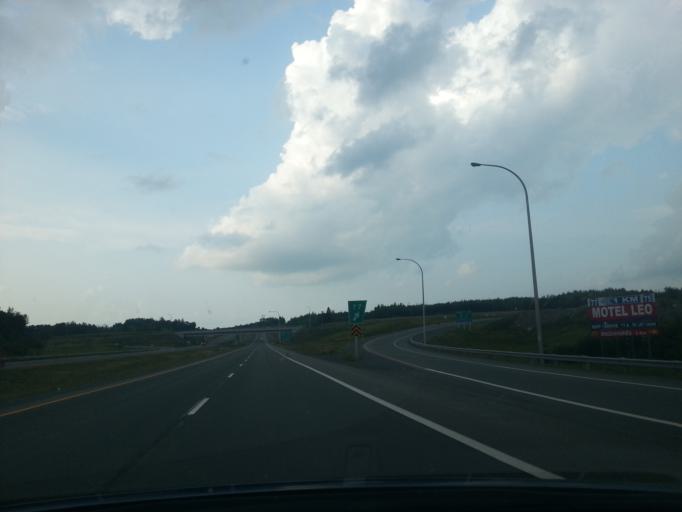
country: US
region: Maine
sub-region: Aroostook County
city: Limestone
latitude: 47.0602
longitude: -67.7642
